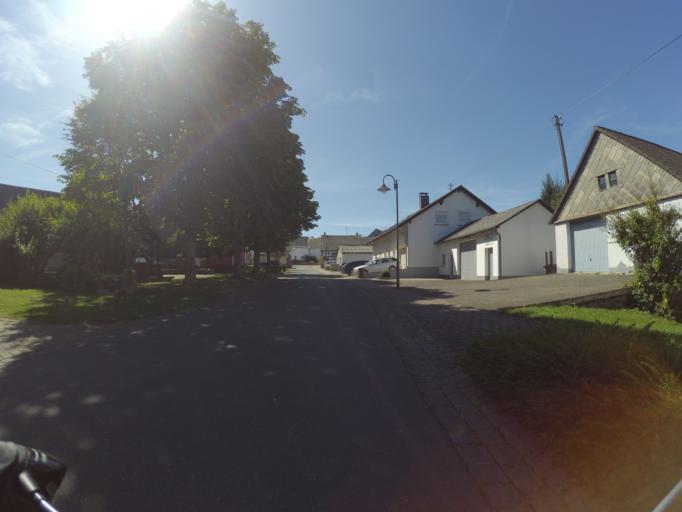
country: DE
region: Rheinland-Pfalz
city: Morbach
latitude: 49.8065
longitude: 7.0730
